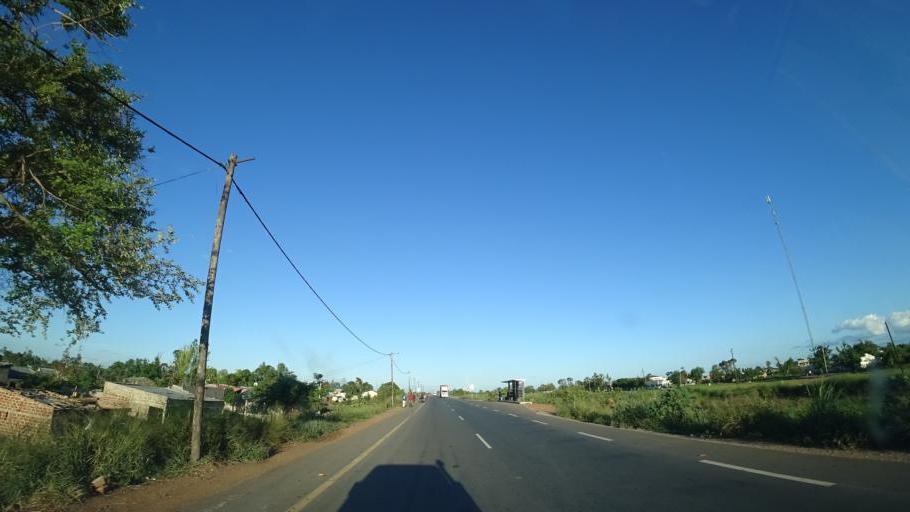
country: MZ
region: Sofala
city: Dondo
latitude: -19.3312
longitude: 34.3155
